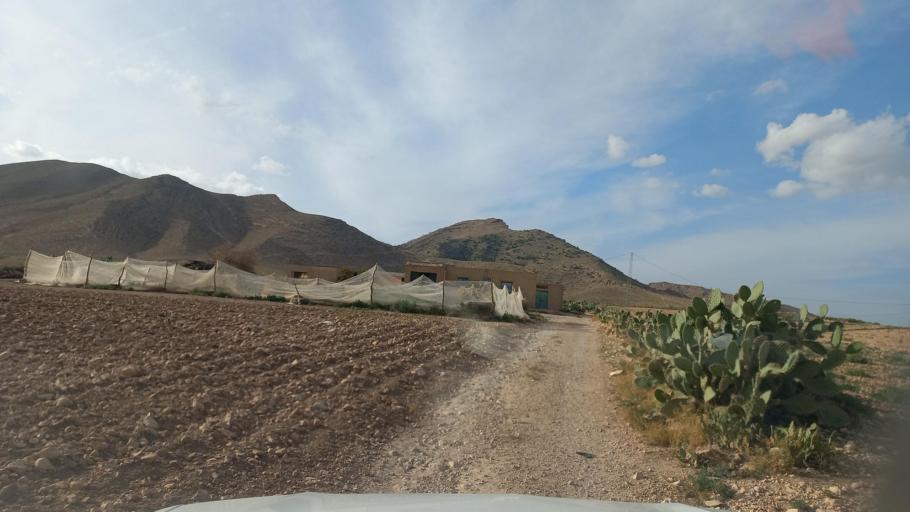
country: TN
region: Al Qasrayn
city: Sbiba
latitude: 35.4557
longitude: 9.0785
